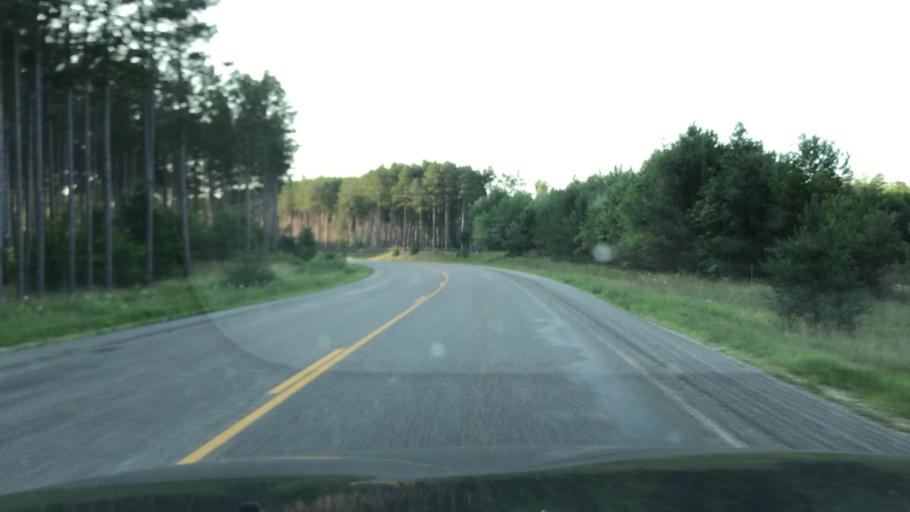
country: US
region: Michigan
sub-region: Osceola County
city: Evart
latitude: 43.8688
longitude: -85.3546
